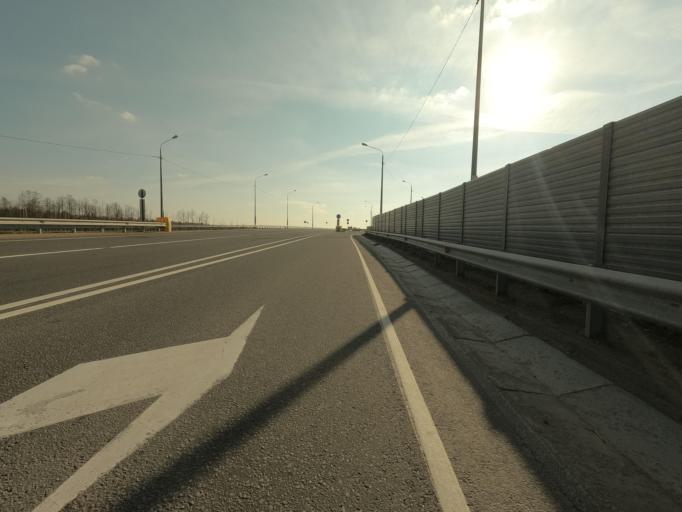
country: RU
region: Leningrad
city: Mga
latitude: 59.7583
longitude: 31.0935
